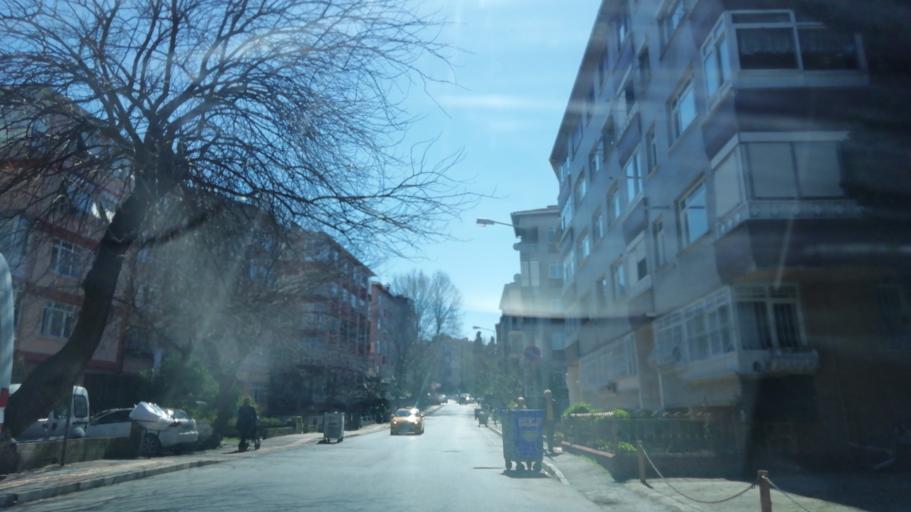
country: TR
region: Istanbul
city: Bahcelievler
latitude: 40.9844
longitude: 28.8670
